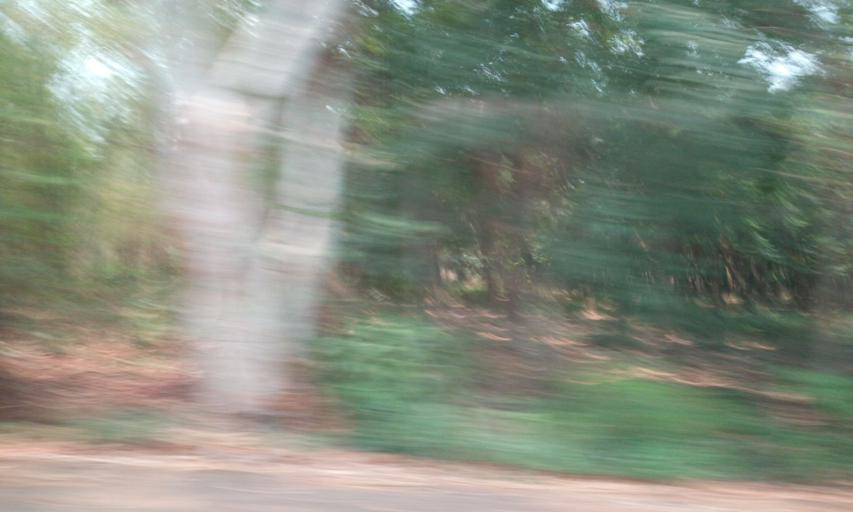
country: TH
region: Phayao
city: Phu Sang
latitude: 19.6117
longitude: 100.3118
